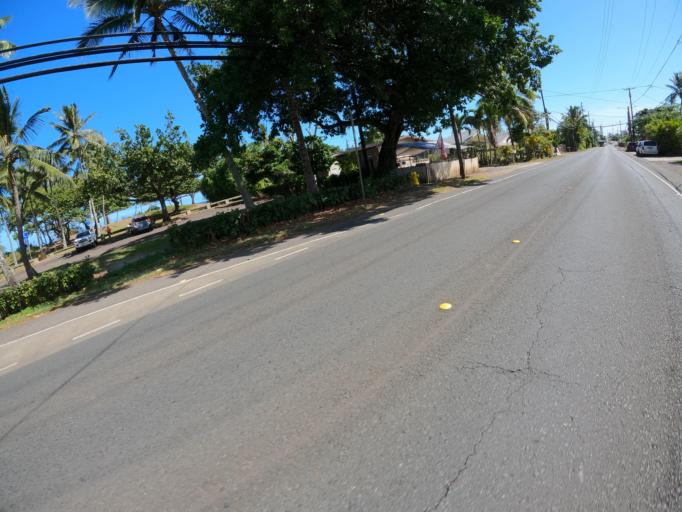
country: US
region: Hawaii
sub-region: Honolulu County
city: Hau'ula
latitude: 21.6225
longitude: -157.9179
